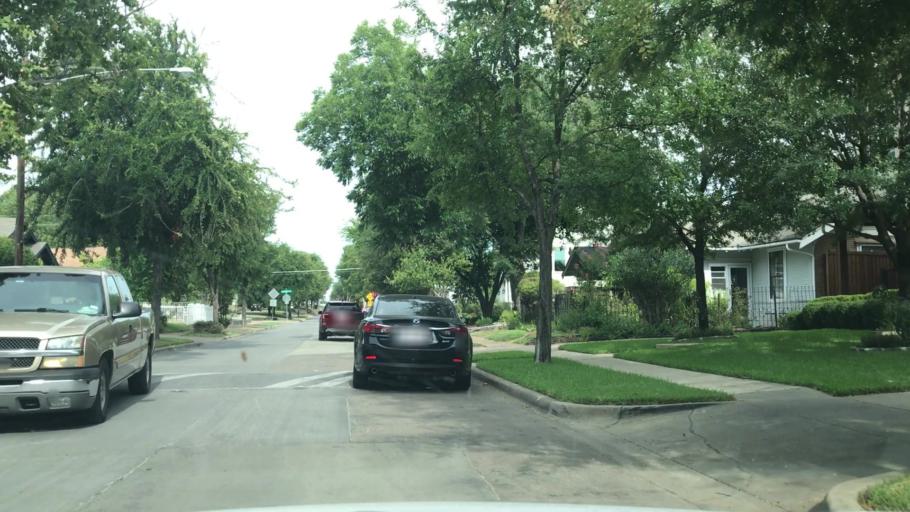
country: US
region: Texas
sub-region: Dallas County
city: Highland Park
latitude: 32.8172
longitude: -96.7758
